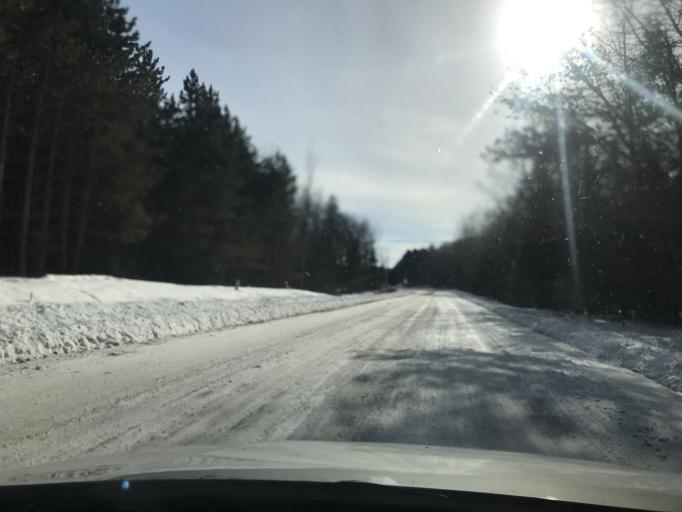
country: US
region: Wisconsin
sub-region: Oconto County
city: Gillett
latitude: 45.1220
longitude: -88.2499
